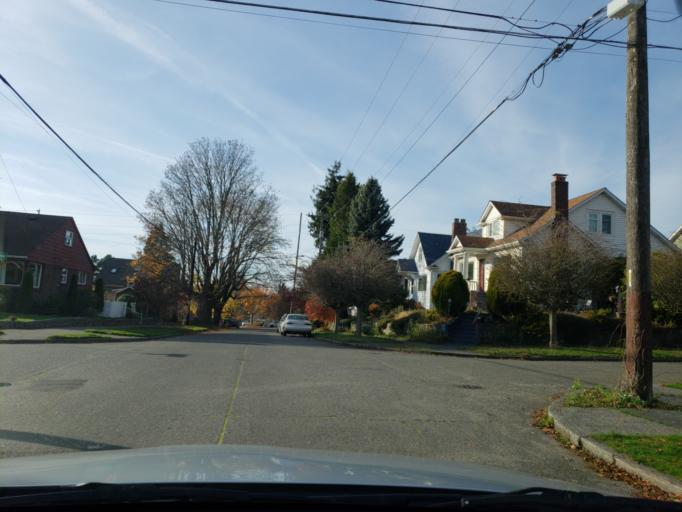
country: US
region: Washington
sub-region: King County
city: Shoreline
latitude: 47.6814
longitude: -122.3692
